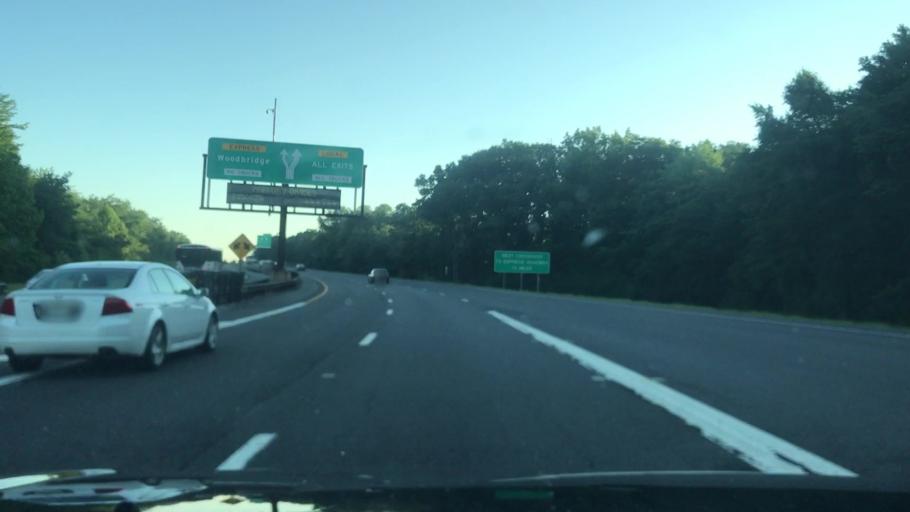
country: US
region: New Jersey
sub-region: Monmouth County
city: Eatontown
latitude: 40.2544
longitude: -74.0802
